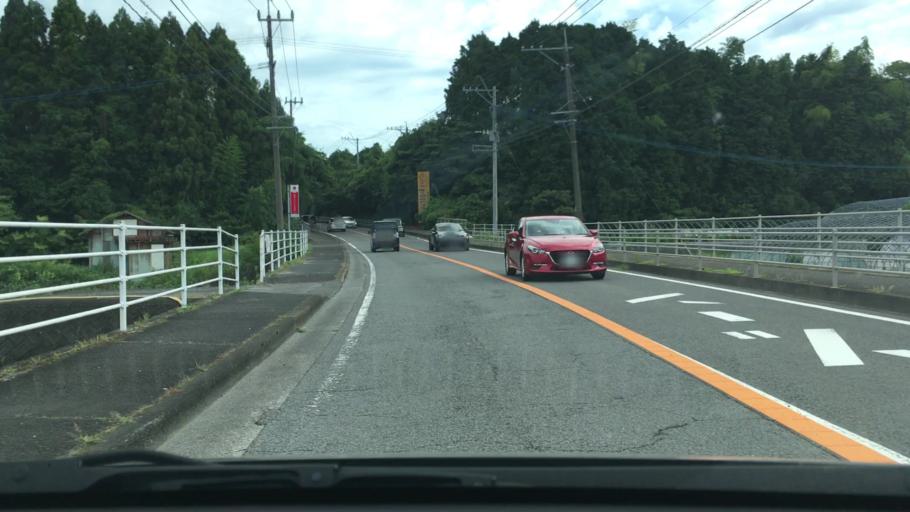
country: JP
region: Nagasaki
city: Togitsu
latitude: 32.9030
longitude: 129.7802
